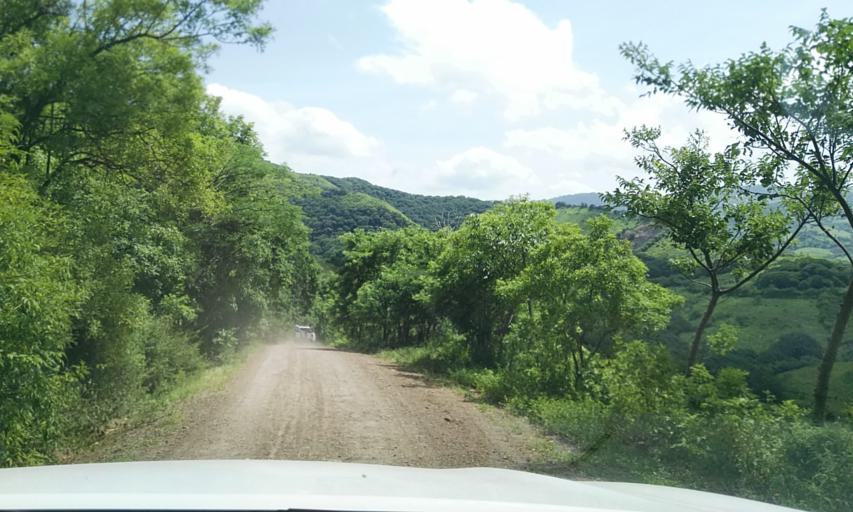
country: NI
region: Matagalpa
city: Terrabona
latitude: 12.6962
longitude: -85.9394
